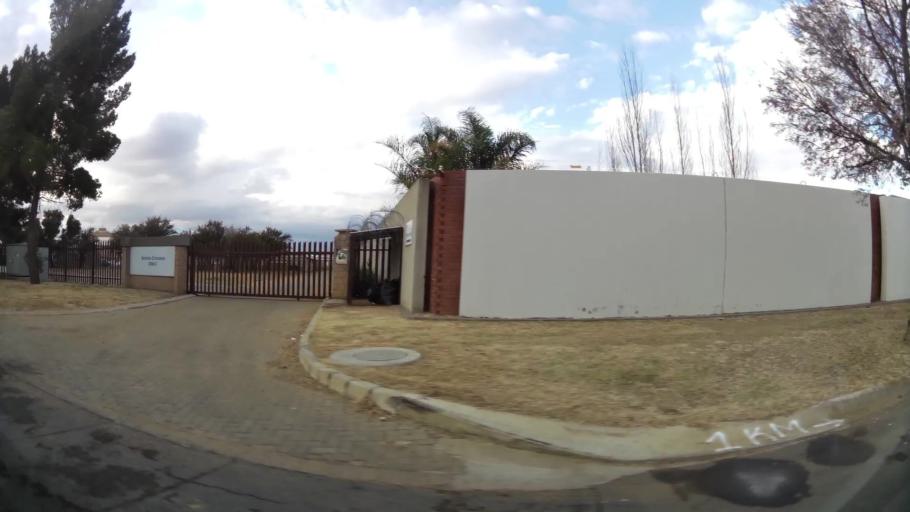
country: ZA
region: Orange Free State
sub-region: Lejweleputswa District Municipality
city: Welkom
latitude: -27.9903
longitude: 26.7310
